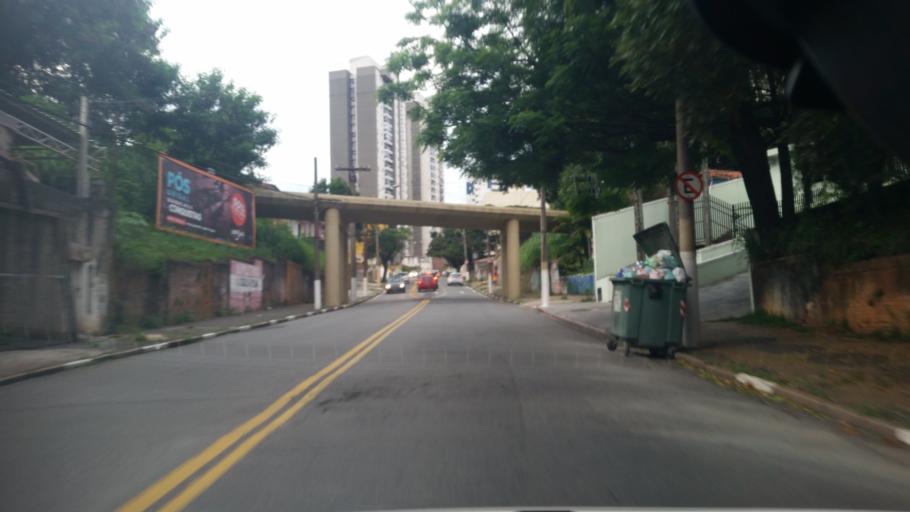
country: BR
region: Sao Paulo
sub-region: Campinas
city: Campinas
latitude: -22.8881
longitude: -47.0575
